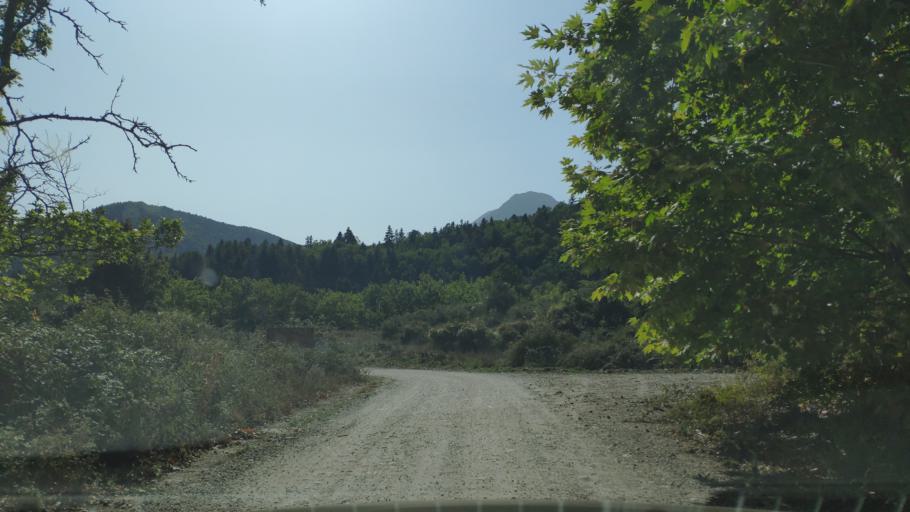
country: GR
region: West Greece
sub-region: Nomos Achaias
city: Aiyira
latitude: 37.9445
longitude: 22.3184
